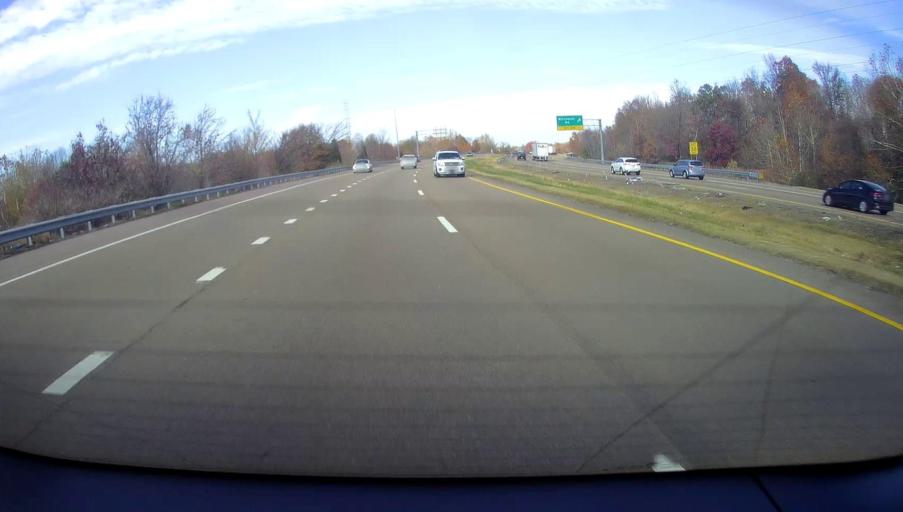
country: US
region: Tennessee
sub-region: Shelby County
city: Germantown
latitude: 35.0447
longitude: -89.8067
